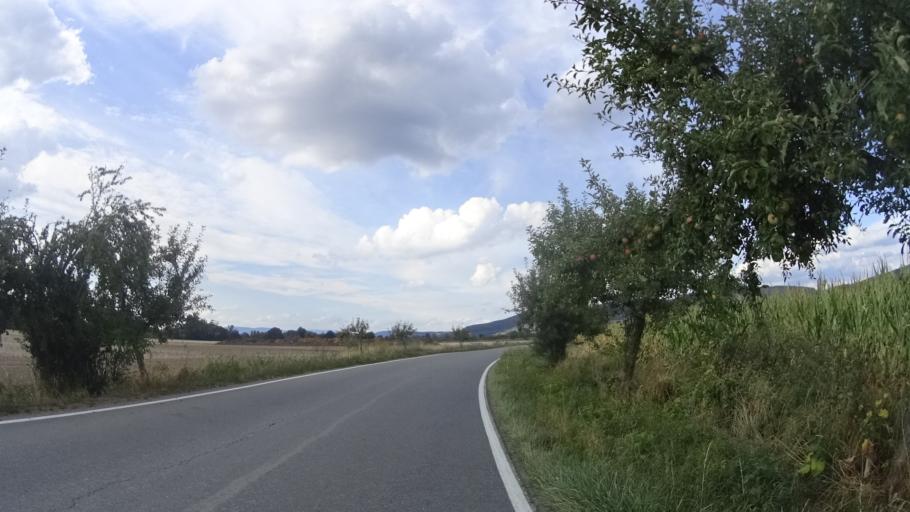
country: CZ
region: Olomoucky
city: Dubicko
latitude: 49.8348
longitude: 16.9358
